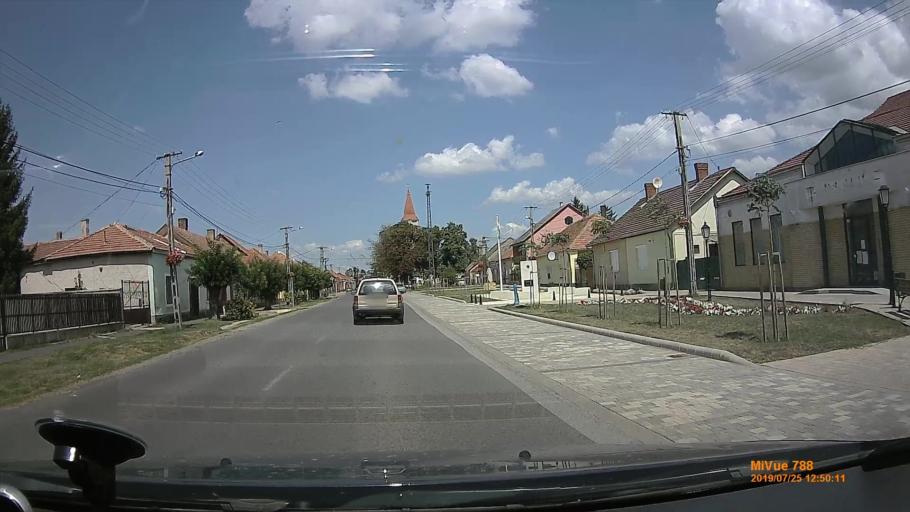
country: HU
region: Borsod-Abauj-Zemplen
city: Abaujszanto
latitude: 48.2787
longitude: 21.1864
